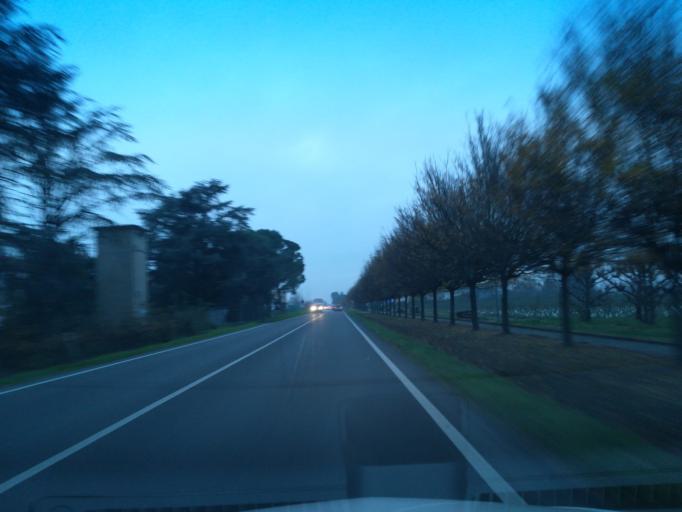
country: IT
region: Emilia-Romagna
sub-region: Provincia di Ravenna
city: Faenza
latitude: 44.2988
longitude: 11.8514
